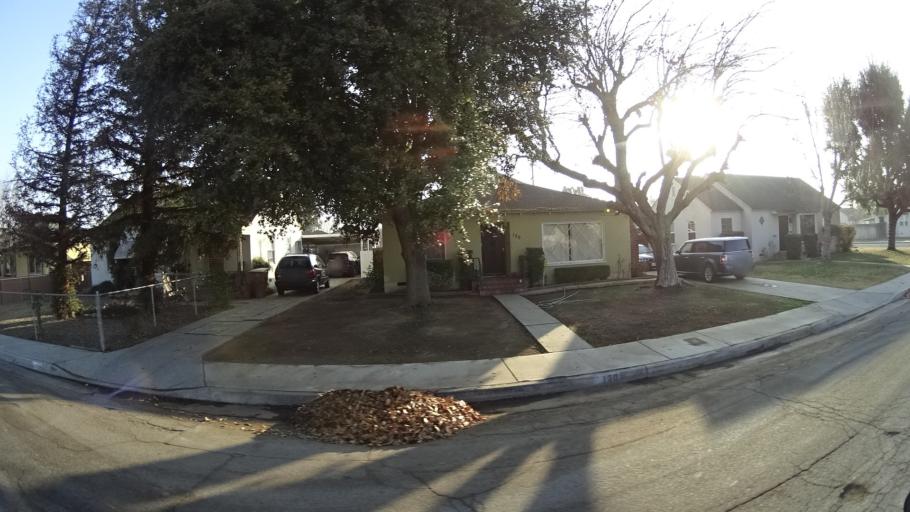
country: US
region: California
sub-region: Kern County
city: Bakersfield
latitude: 35.3565
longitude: -119.0425
